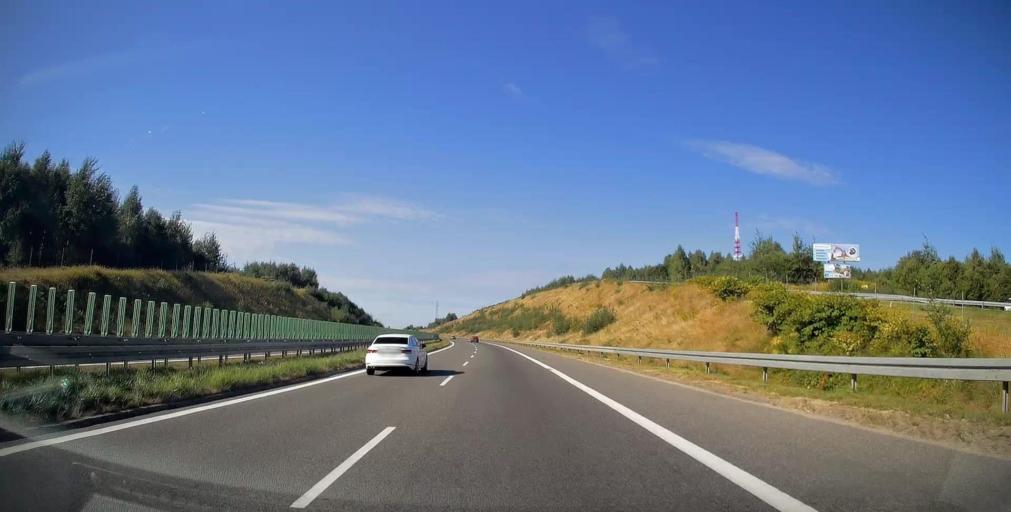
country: PL
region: Swietokrzyskie
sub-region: Powiat skarzyski
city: Laczna
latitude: 50.9841
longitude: 20.7545
